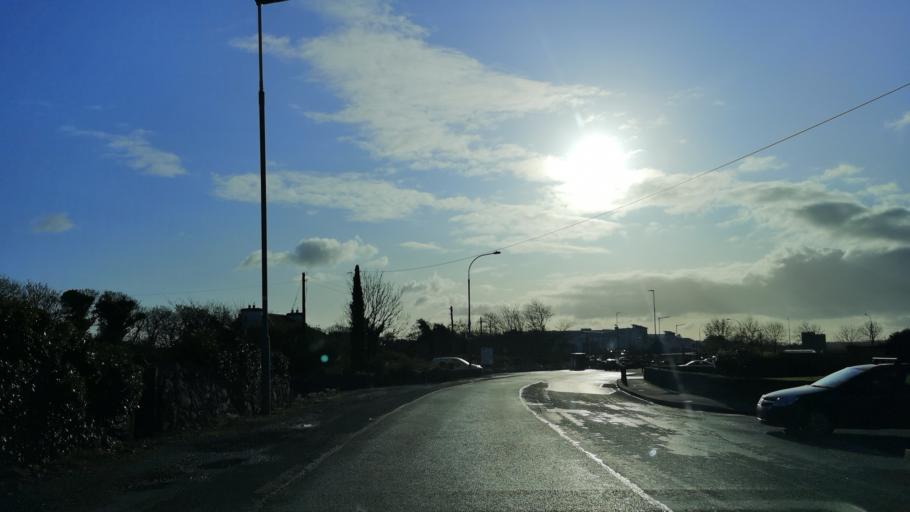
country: IE
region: Connaught
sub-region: County Galway
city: Oranmore
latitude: 53.2736
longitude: -8.9280
